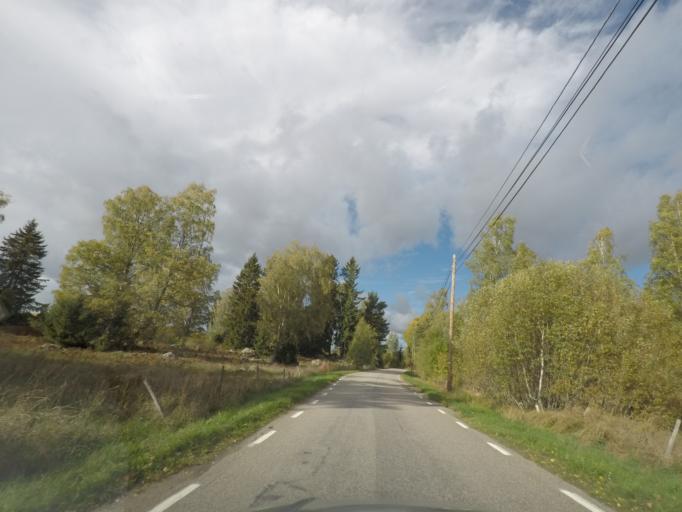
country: SE
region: Soedermanland
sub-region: Eskilstuna Kommun
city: Kvicksund
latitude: 59.3189
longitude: 16.2692
